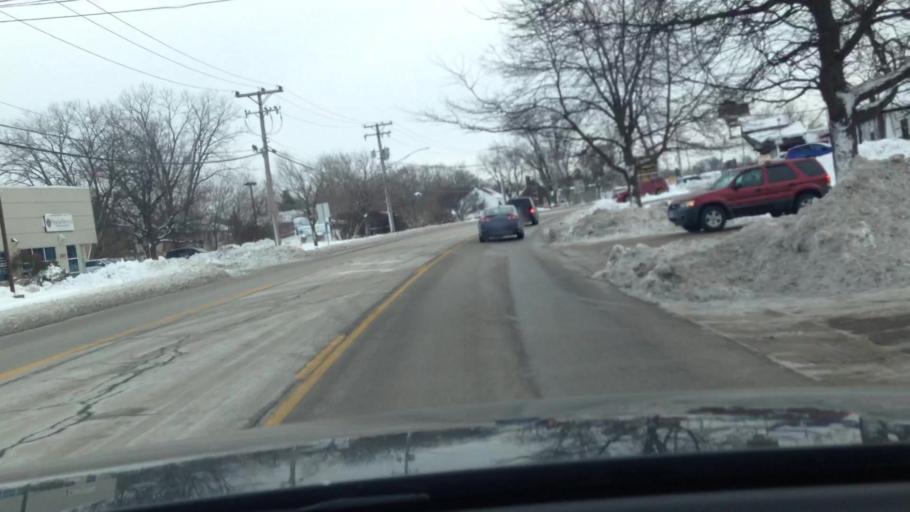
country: US
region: Illinois
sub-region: McHenry County
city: Woodstock
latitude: 42.3082
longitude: -88.4316
